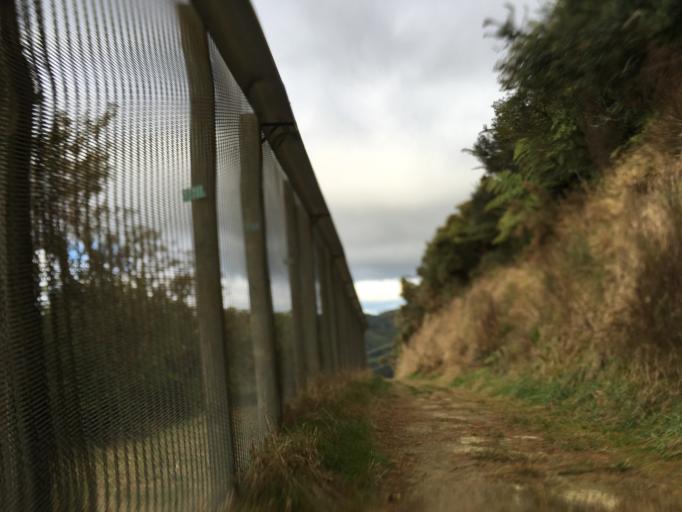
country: NZ
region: Wellington
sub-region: Wellington City
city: Brooklyn
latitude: -41.2990
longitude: 174.7384
